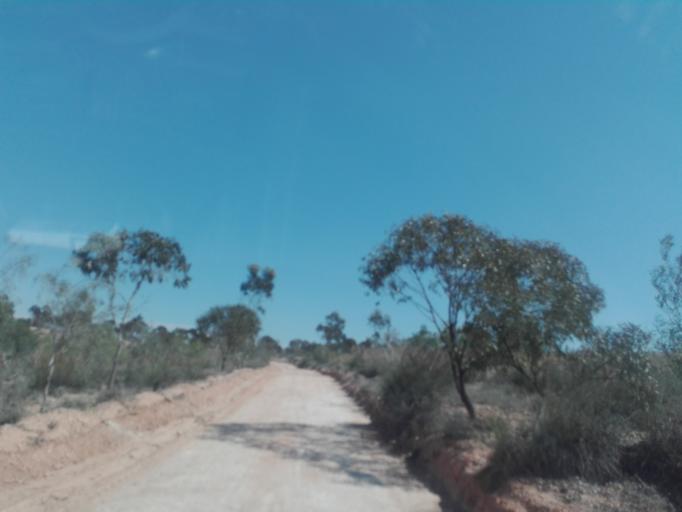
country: TN
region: Safaqis
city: Sfax
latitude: 34.6989
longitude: 10.5305
